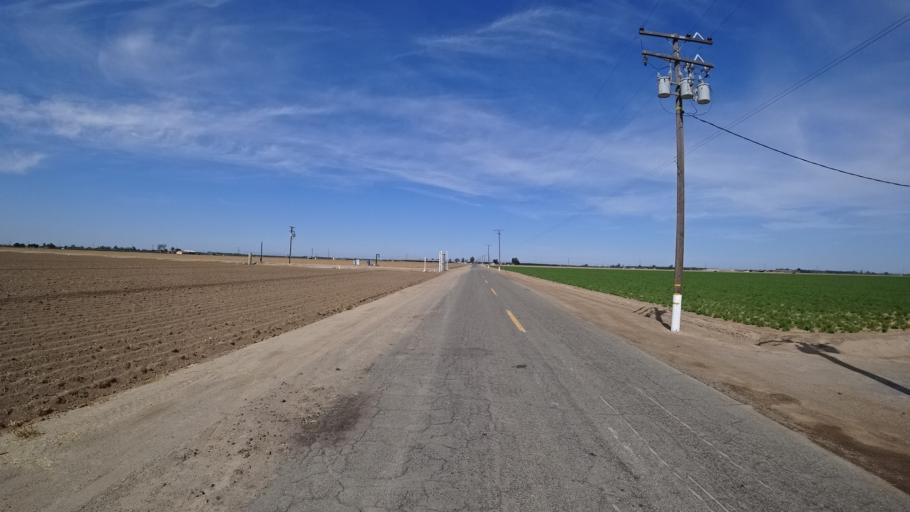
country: US
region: California
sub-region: Kings County
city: Hanford
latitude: 36.3574
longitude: -119.5606
